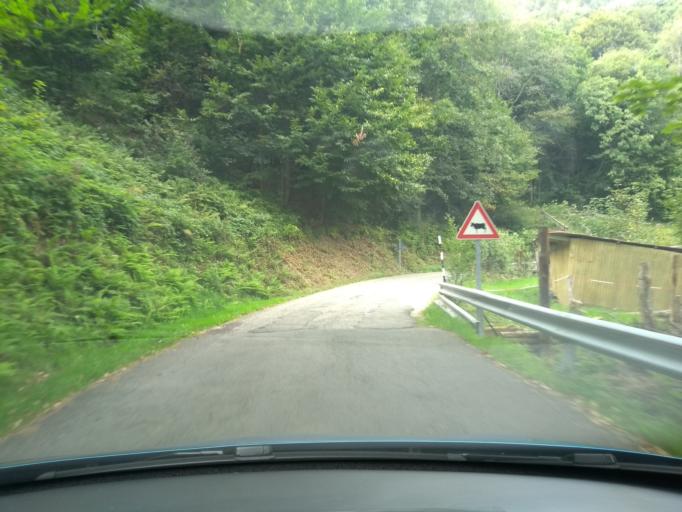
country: IT
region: Piedmont
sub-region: Provincia di Torino
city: Corio
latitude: 45.3268
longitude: 7.5175
